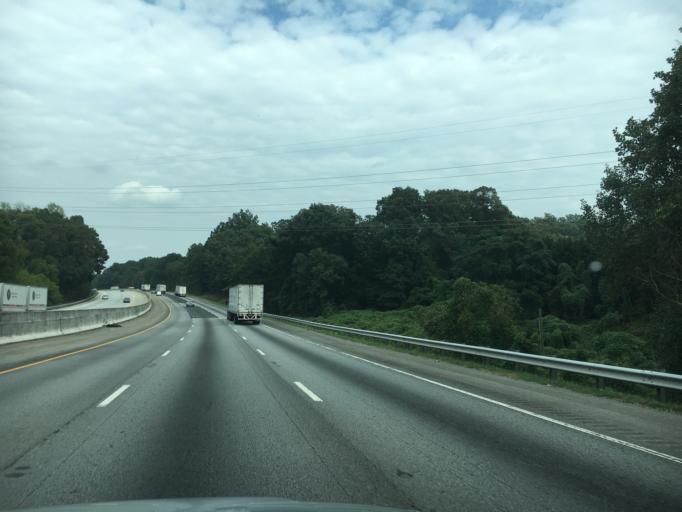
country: US
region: South Carolina
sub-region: Anderson County
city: Northlake
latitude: 34.6073
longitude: -82.6342
